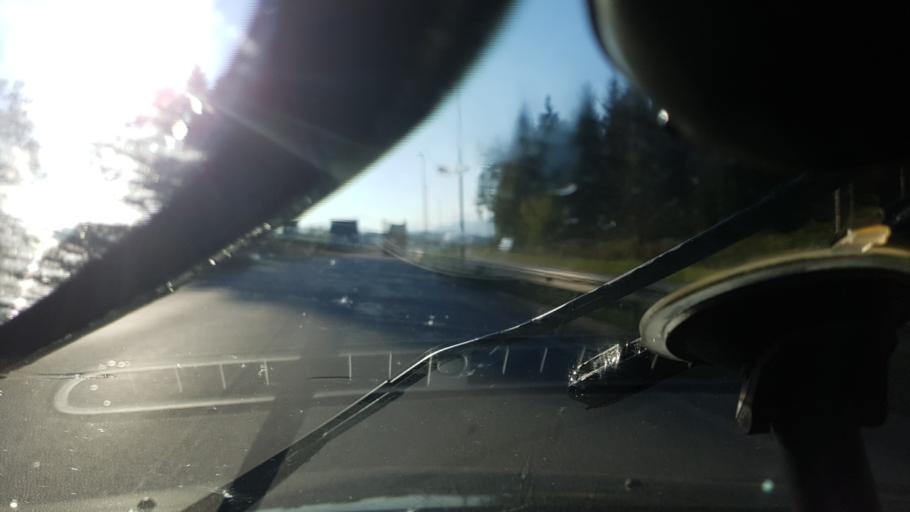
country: SI
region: Sencur
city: Sencur
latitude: 46.2351
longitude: 14.4471
